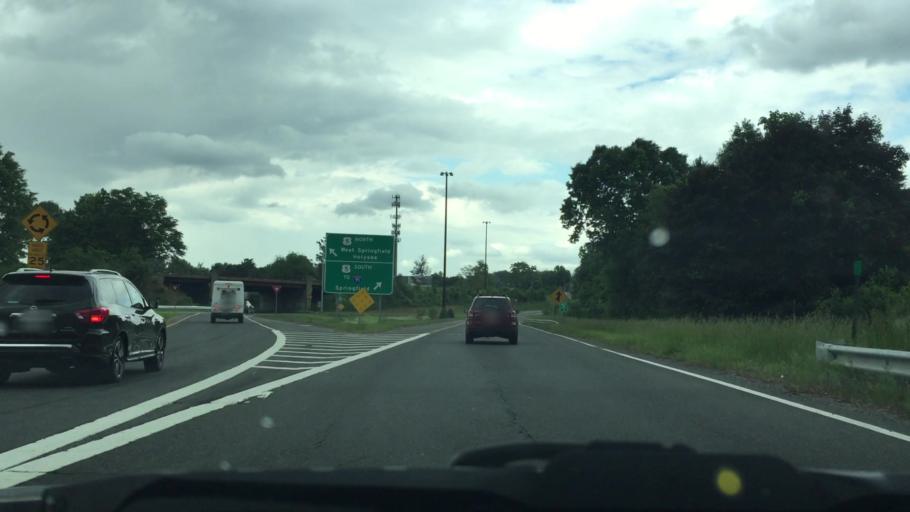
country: US
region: Massachusetts
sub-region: Hampden County
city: Springfield
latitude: 42.0795
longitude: -72.5904
